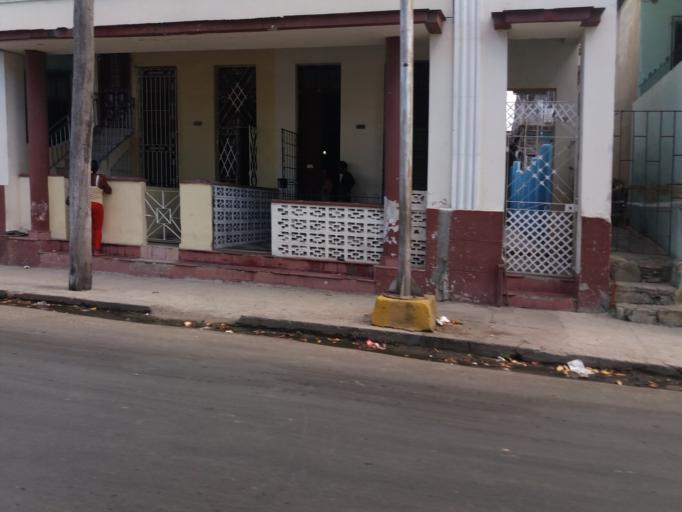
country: CU
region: Cienfuegos
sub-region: Municipio de Cienfuegos
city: Cienfuegos
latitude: 22.1490
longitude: -80.4456
